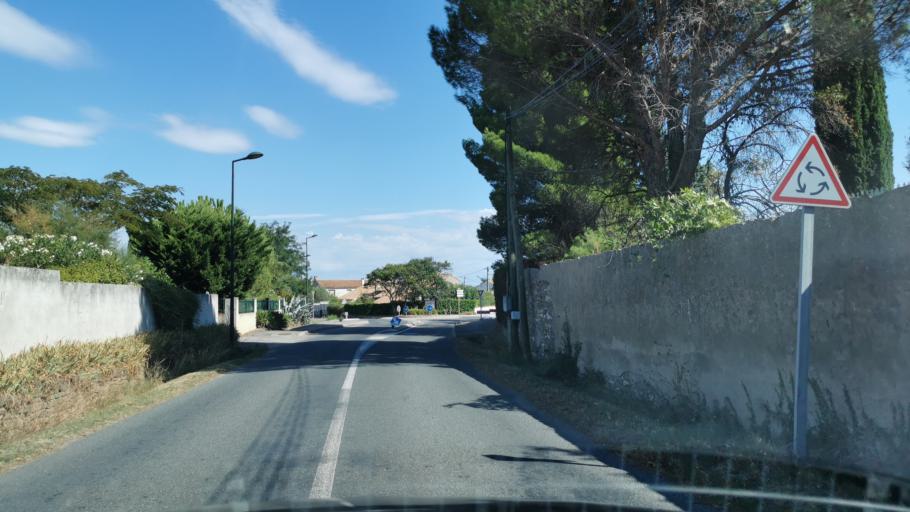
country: FR
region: Languedoc-Roussillon
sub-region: Departement de l'Aude
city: Peyriac-Minervois
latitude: 43.3133
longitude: 2.5561
